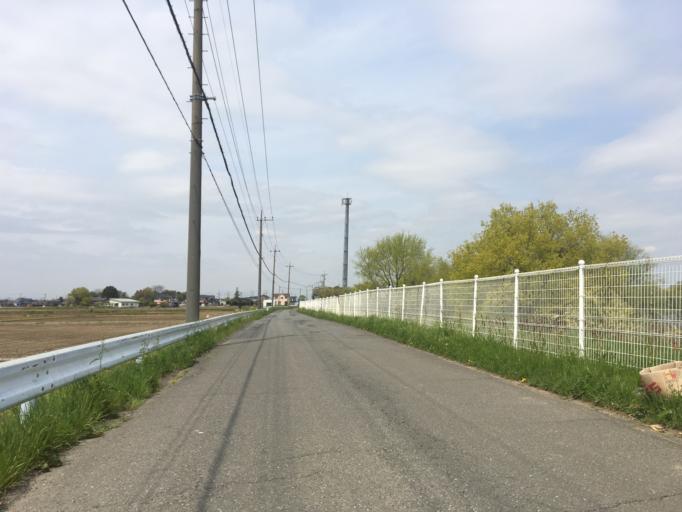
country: JP
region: Saitama
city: Kamifukuoka
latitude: 35.8856
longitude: 139.5491
